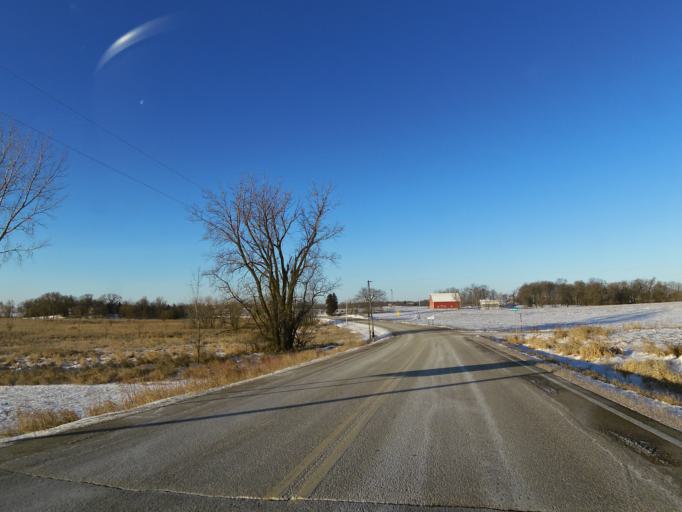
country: US
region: Minnesota
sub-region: Scott County
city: Jordan
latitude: 44.6633
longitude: -93.5411
